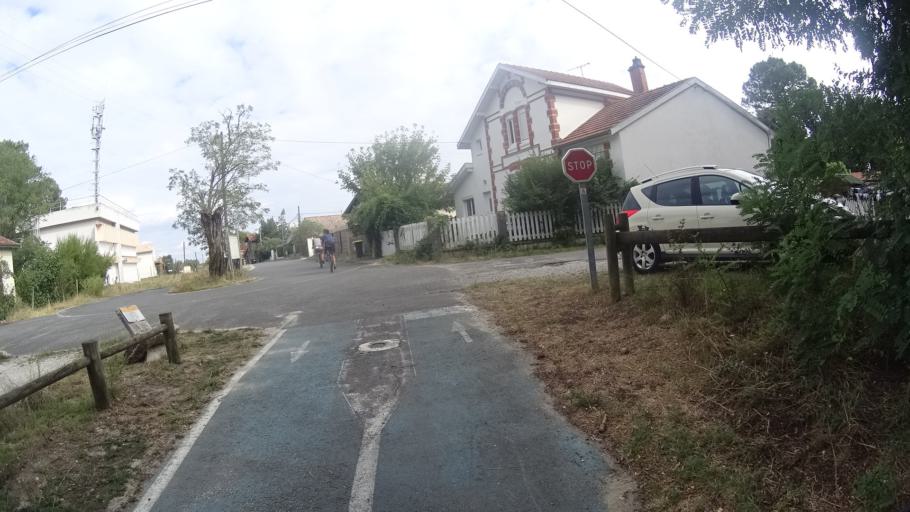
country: FR
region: Aquitaine
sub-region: Departement de la Gironde
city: Lacanau
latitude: 45.0035
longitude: -1.1370
